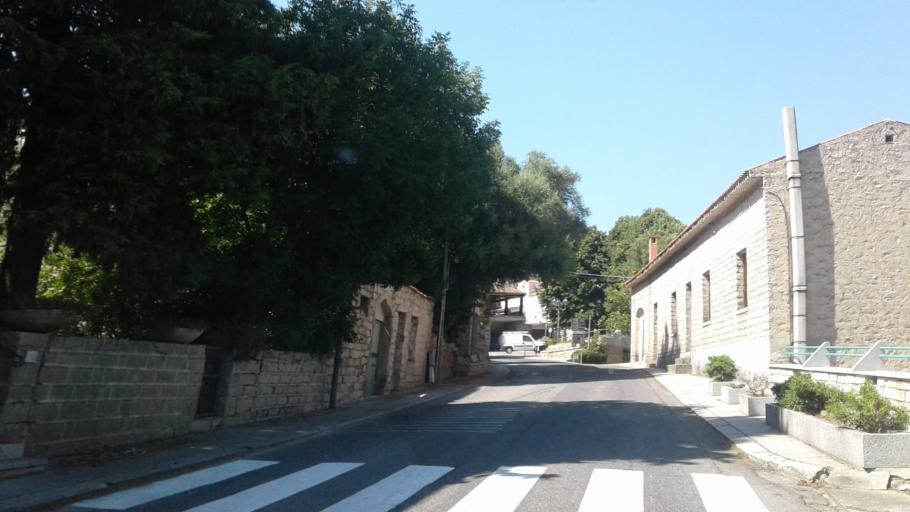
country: IT
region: Sardinia
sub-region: Provincia di Olbia-Tempio
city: Aggius
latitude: 40.9274
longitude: 9.0636
